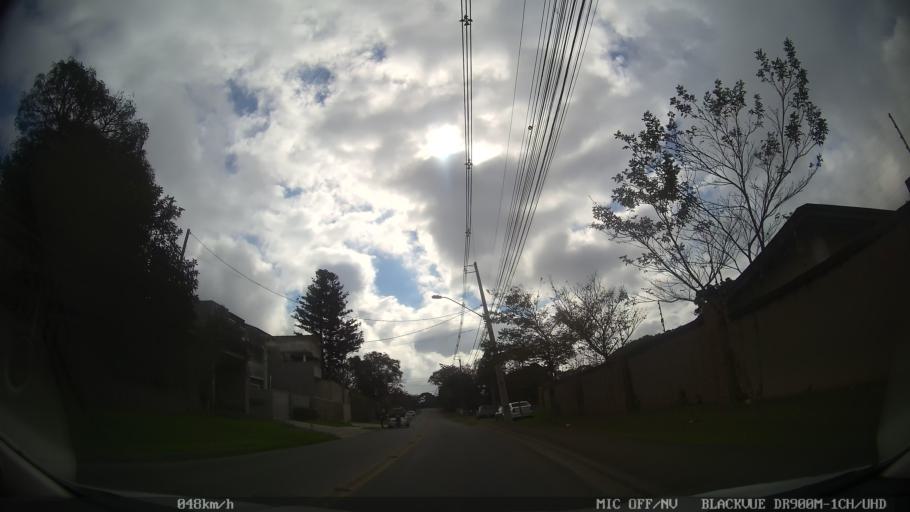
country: BR
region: Parana
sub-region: Curitiba
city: Curitiba
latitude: -25.3626
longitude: -49.2487
